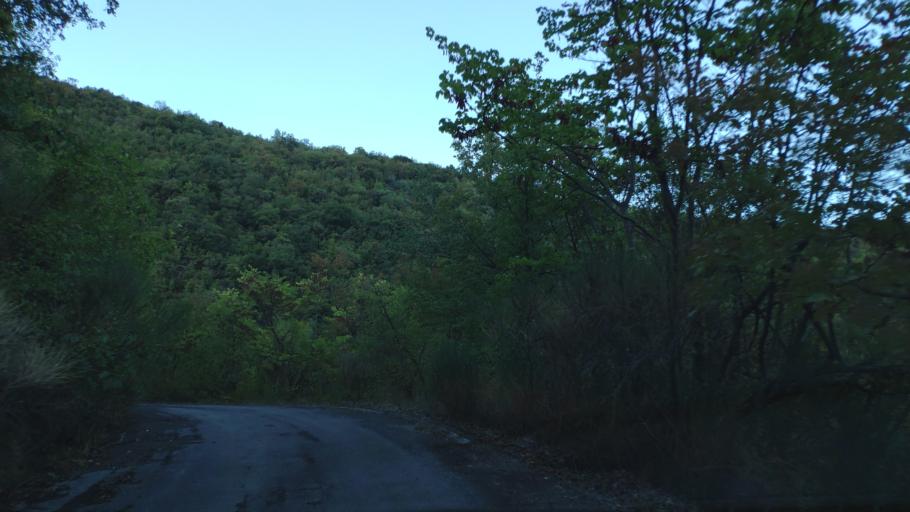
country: GR
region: Peloponnese
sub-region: Nomos Arkadias
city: Dimitsana
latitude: 37.5606
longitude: 22.0430
